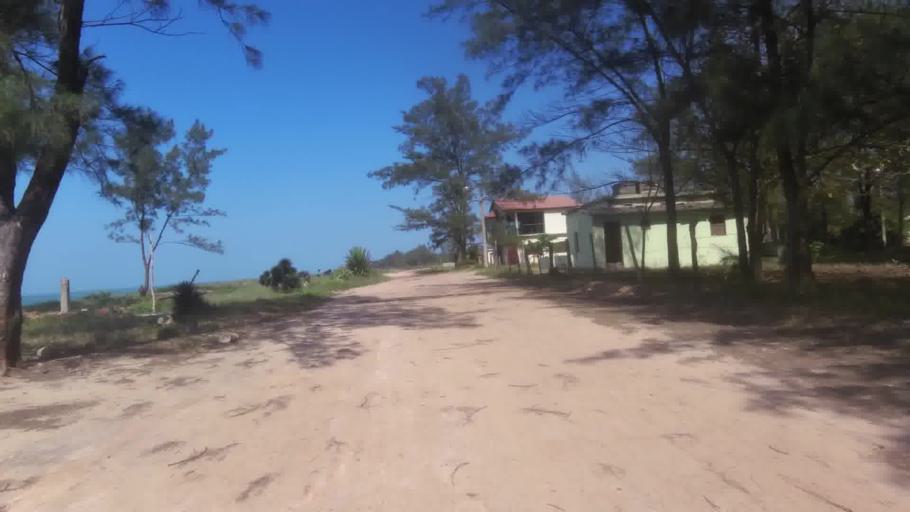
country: BR
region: Espirito Santo
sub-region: Marataizes
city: Marataizes
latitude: -21.1124
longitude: -40.8542
